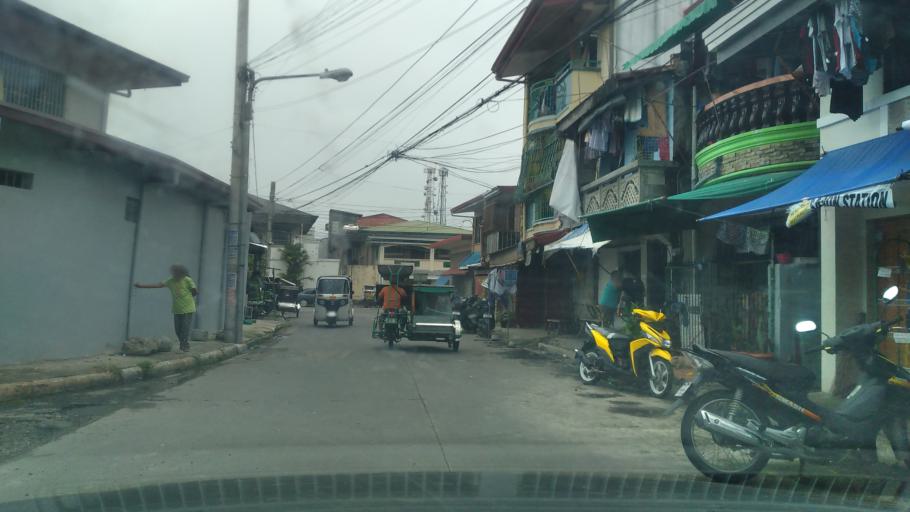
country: PH
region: Calabarzon
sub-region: Province of Quezon
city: Lucena
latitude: 13.9357
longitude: 121.6166
